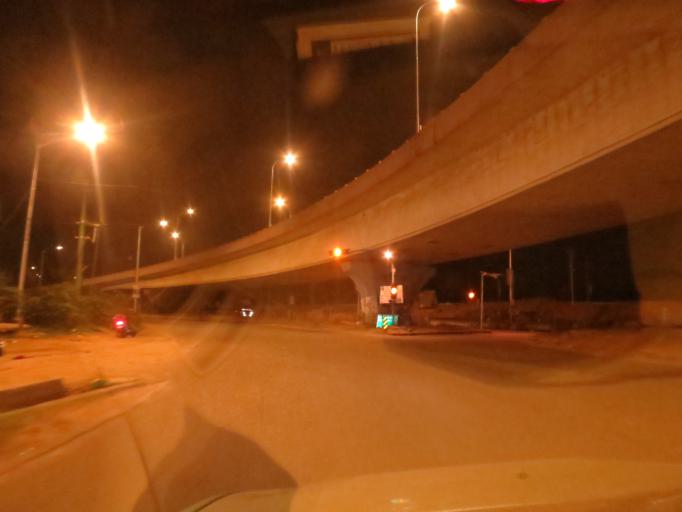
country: IN
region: Karnataka
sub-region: Bangalore Urban
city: Bangalore
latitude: 12.9999
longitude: 77.6814
